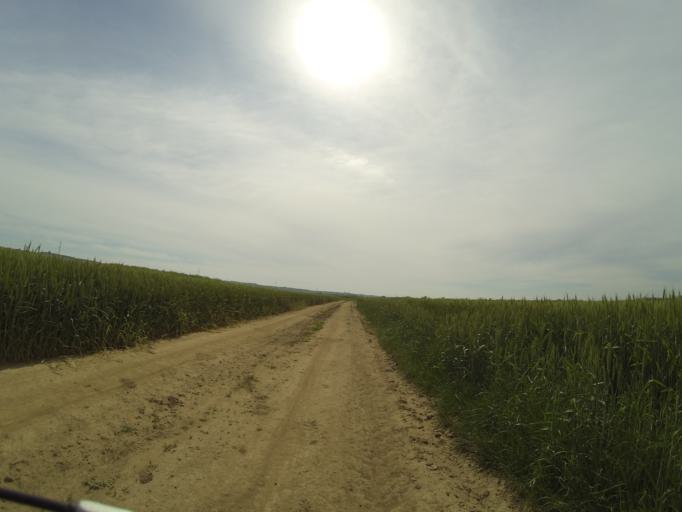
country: RO
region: Dolj
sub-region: Comuna Malu Mare
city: Preajba
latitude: 44.2683
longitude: 23.8607
